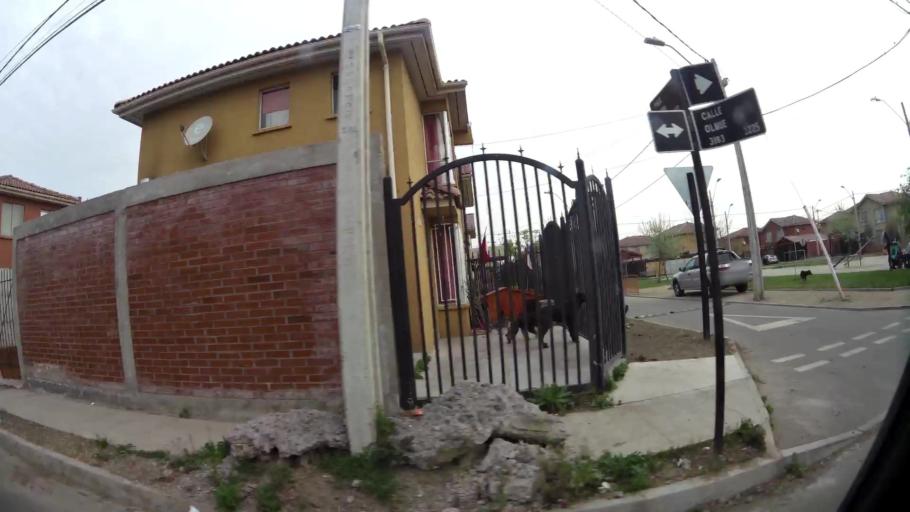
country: CL
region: Santiago Metropolitan
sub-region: Provincia de Talagante
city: Penaflor
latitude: -33.5323
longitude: -70.7973
